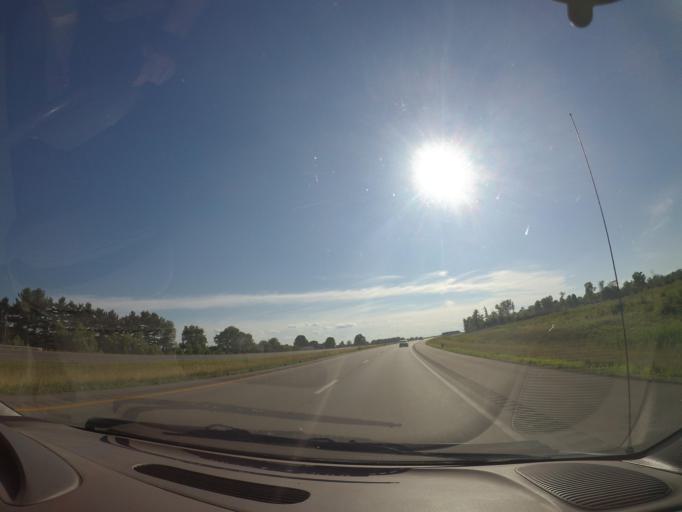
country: US
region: Ohio
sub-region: Henry County
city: Liberty Center
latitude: 41.4291
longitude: -83.9917
